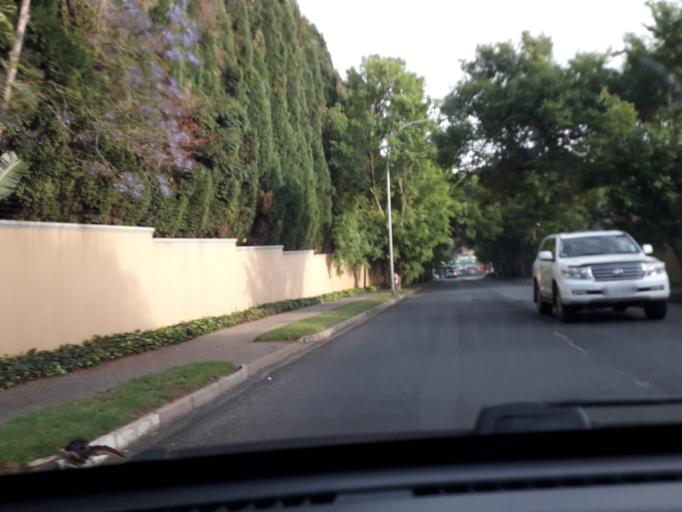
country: ZA
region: Gauteng
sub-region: City of Johannesburg Metropolitan Municipality
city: Johannesburg
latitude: -26.1492
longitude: 28.0630
